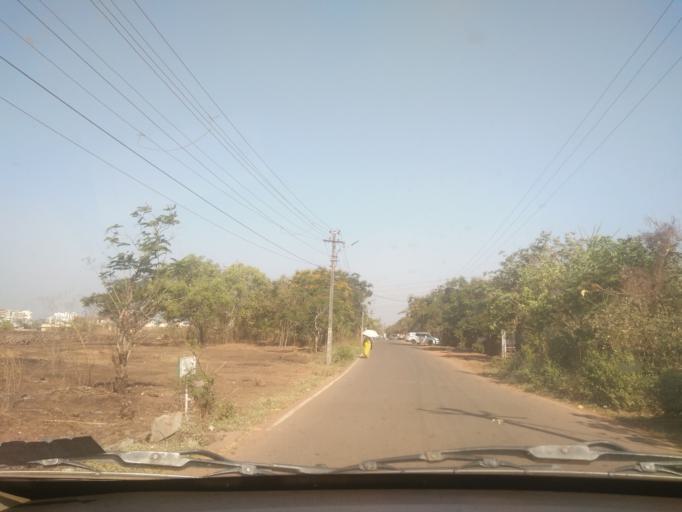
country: IN
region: Goa
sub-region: South Goa
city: Chicalim
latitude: 15.3910
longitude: 73.8638
